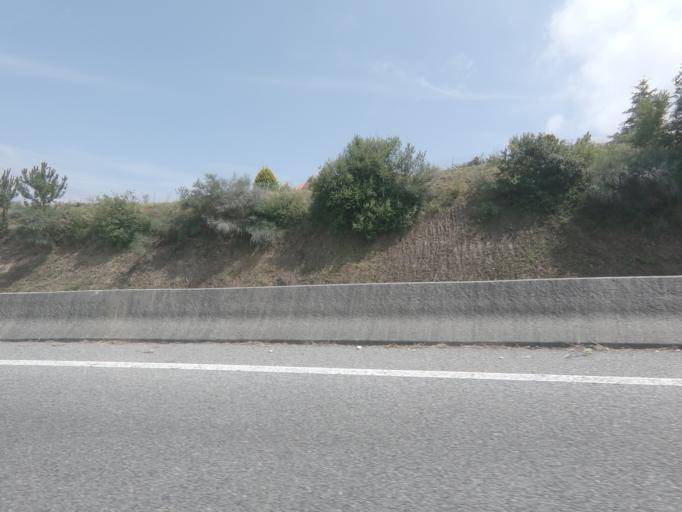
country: ES
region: Galicia
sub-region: Provincia de Pontevedra
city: Baiona
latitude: 42.0993
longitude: -8.8251
